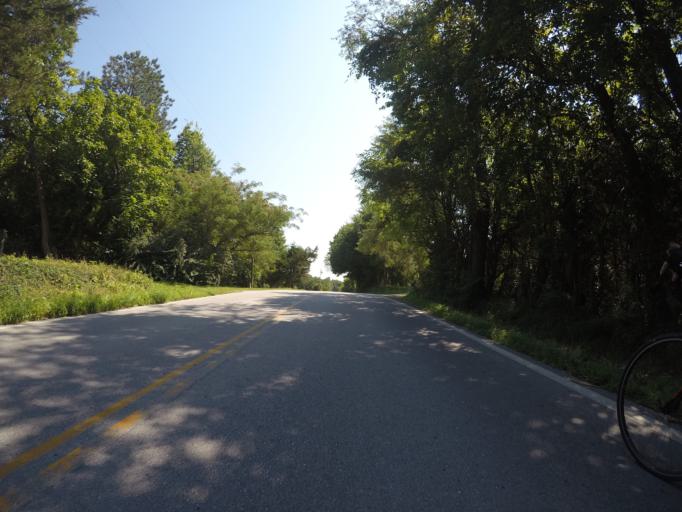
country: US
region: Kansas
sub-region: Leavenworth County
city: Lansing
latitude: 39.2223
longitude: -94.8631
